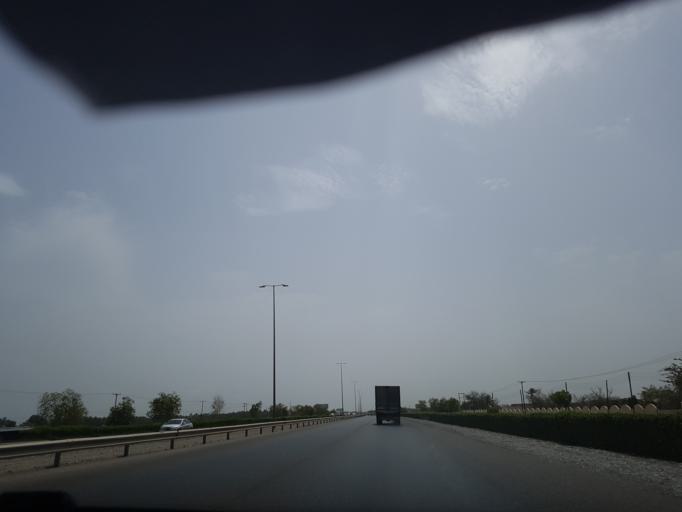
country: OM
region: Al Batinah
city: Barka'
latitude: 23.7365
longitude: 57.6612
